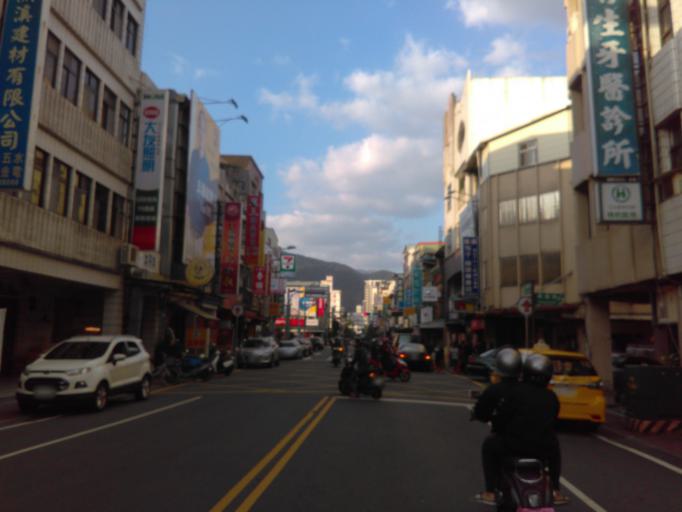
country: TW
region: Taiwan
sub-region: Yilan
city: Yilan
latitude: 24.8202
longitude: 121.7707
